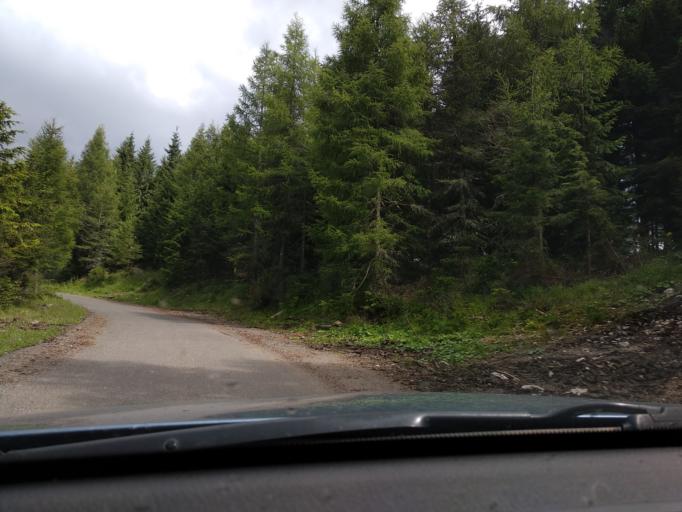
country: SK
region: Zilinsky
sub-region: Okres Liptovsky Mikulas
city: Hybe
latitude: 49.0183
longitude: 19.9018
